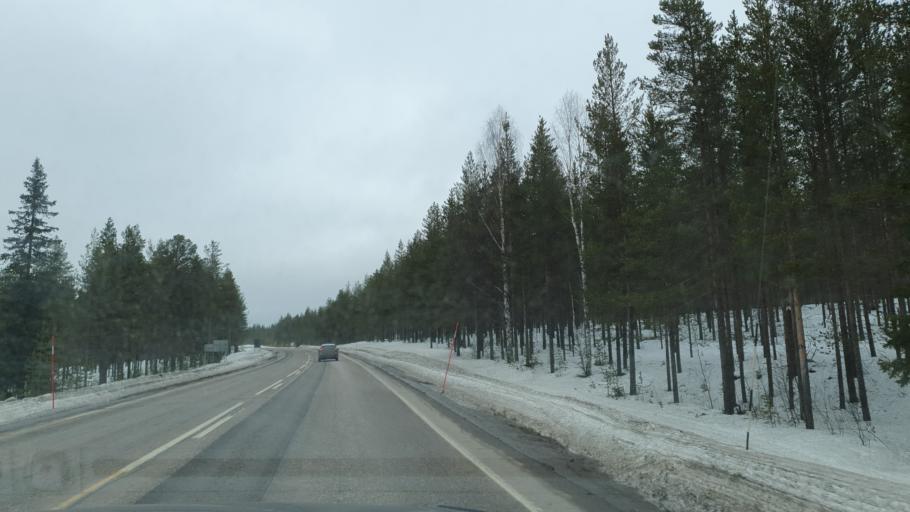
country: FI
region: Lapland
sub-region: Torniolaakso
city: Pello
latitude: 66.9172
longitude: 24.0932
